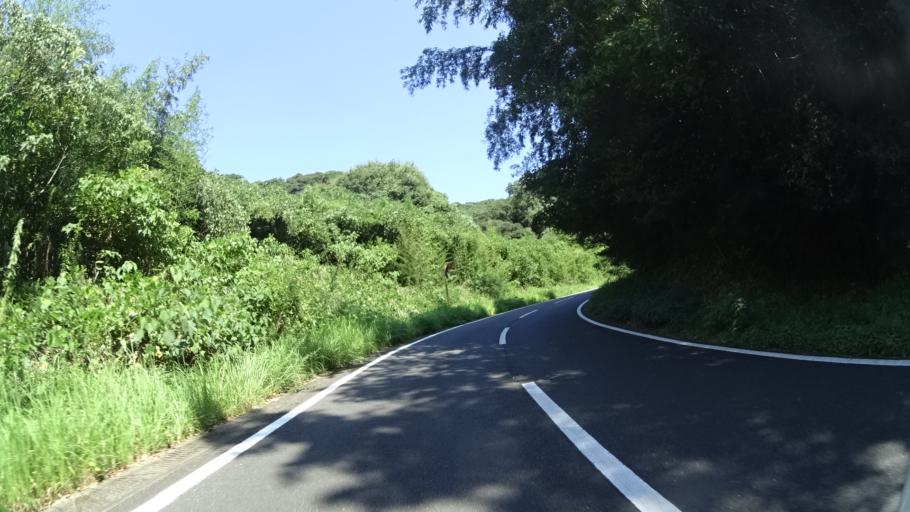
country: JP
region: Kagoshima
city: Kajiki
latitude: 31.7547
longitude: 130.6681
